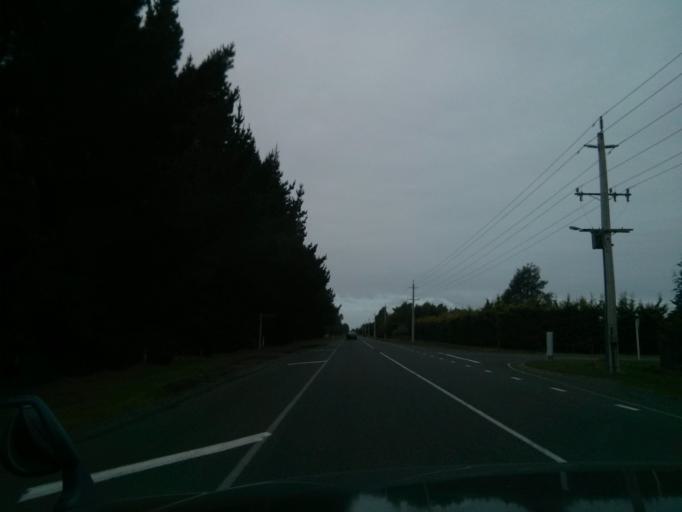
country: NZ
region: Canterbury
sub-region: Waimakariri District
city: Kaiapoi
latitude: -43.3755
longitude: 172.5205
